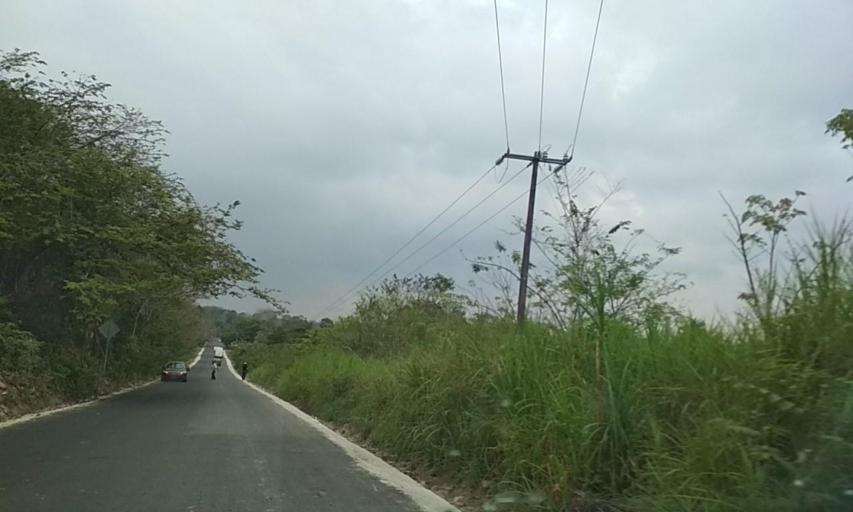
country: MX
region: Tabasco
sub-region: Huimanguillo
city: Francisco Rueda
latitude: 17.7307
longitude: -94.1025
